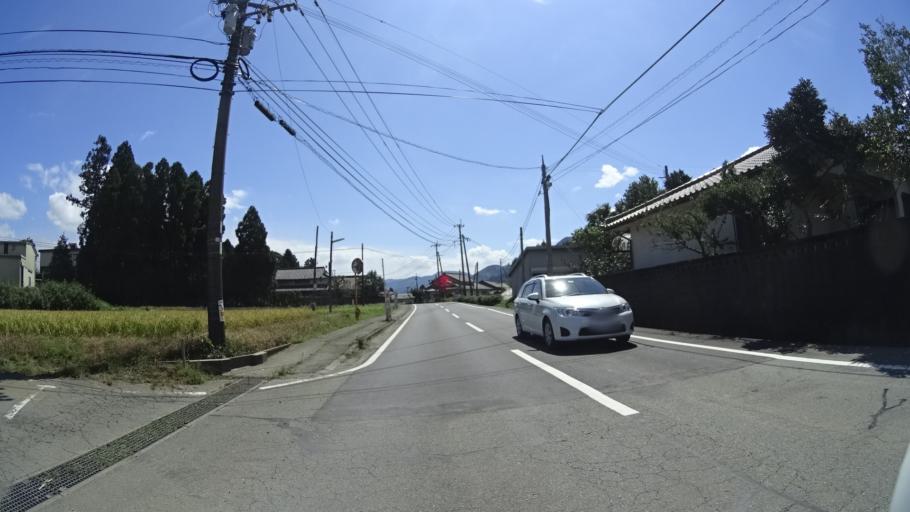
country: JP
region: Kumamoto
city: Aso
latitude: 32.9211
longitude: 130.9938
